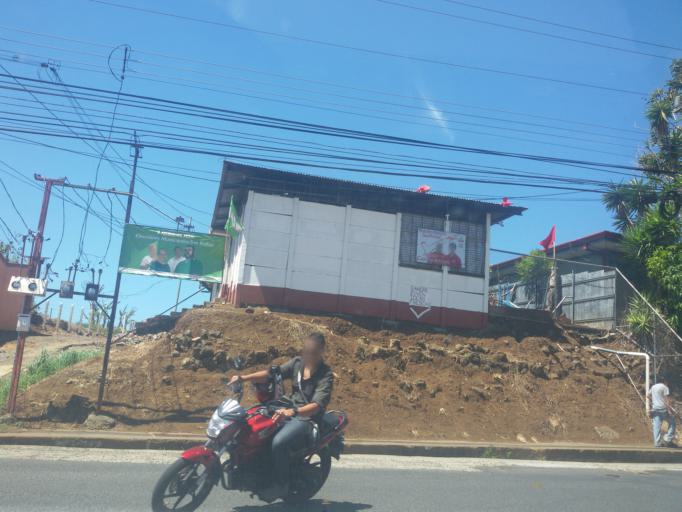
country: CR
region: Heredia
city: San Rafael
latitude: 10.0090
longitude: -84.1054
